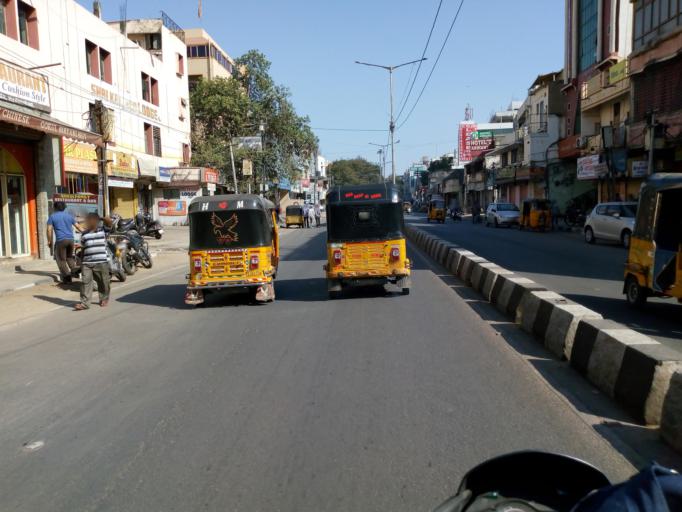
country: IN
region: Telangana
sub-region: Hyderabad
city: Hyderabad
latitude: 17.3903
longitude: 78.4921
